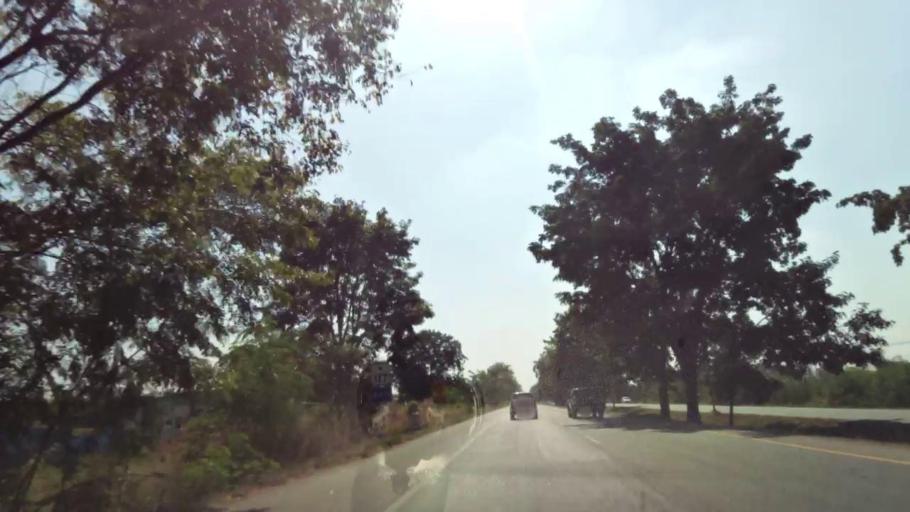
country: TH
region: Phichit
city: Wachira Barami
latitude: 16.4049
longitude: 100.1419
